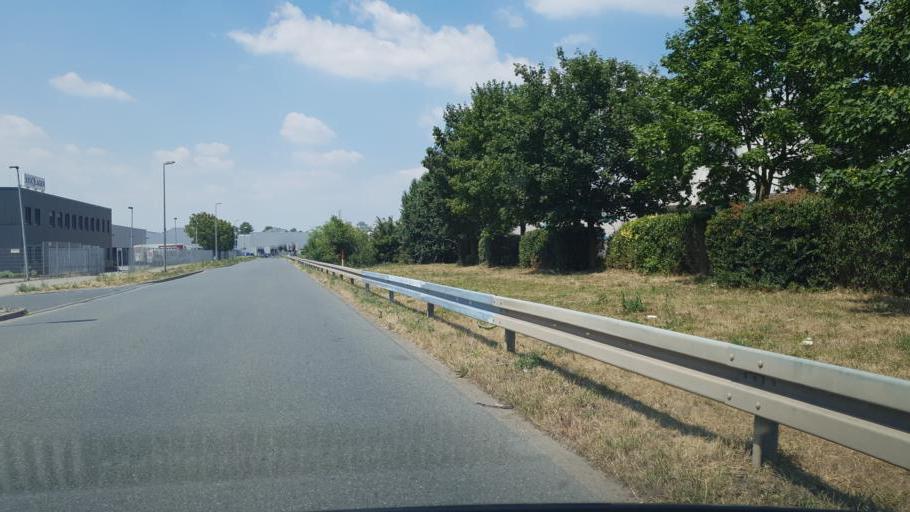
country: DE
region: Hesse
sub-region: Regierungsbezirk Darmstadt
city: Gross-Gerau
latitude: 49.9257
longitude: 8.4938
